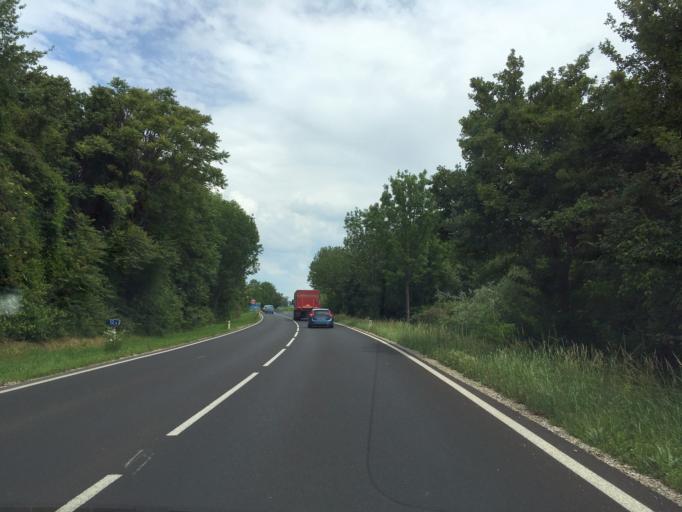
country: AT
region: Lower Austria
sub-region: Politischer Bezirk Modling
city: Laxenburg
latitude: 48.0799
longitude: 16.3584
